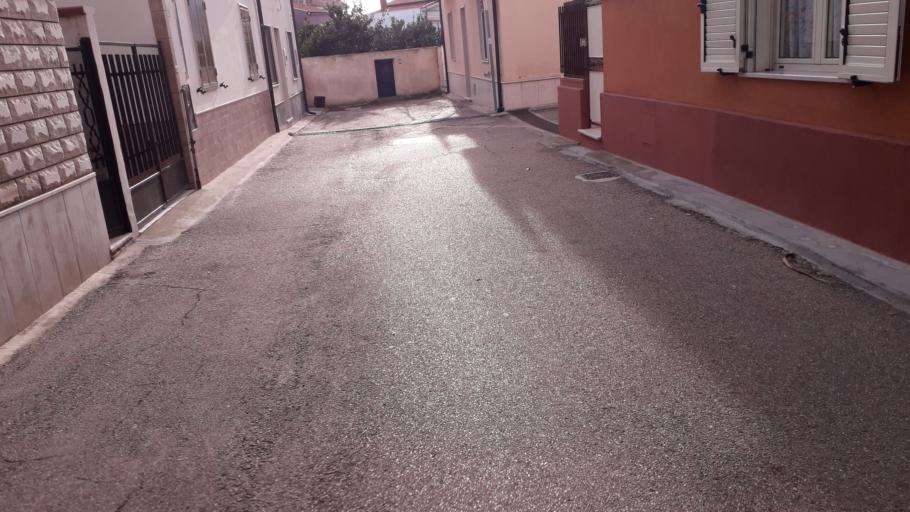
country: IT
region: Molise
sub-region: Provincia di Campobasso
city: Campomarino
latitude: 41.9567
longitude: 15.0342
